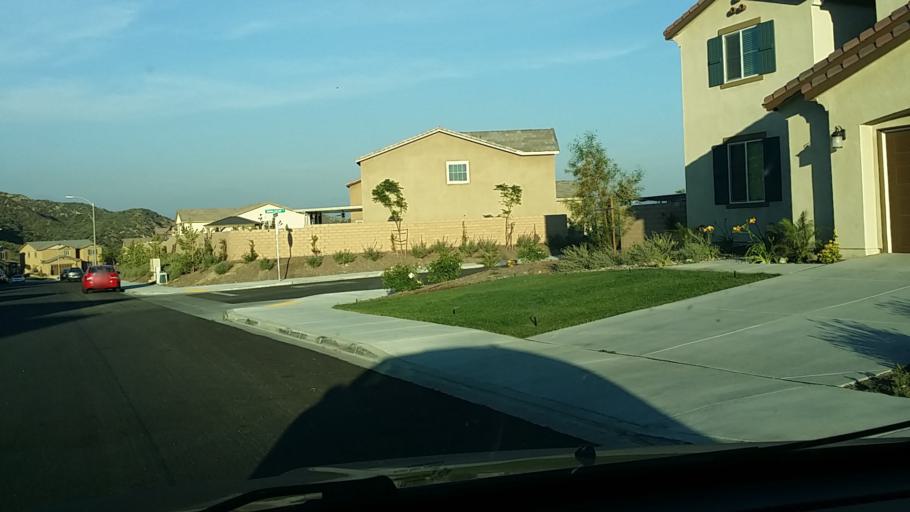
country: US
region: California
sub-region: San Bernardino County
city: Muscoy
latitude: 34.1904
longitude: -117.4140
